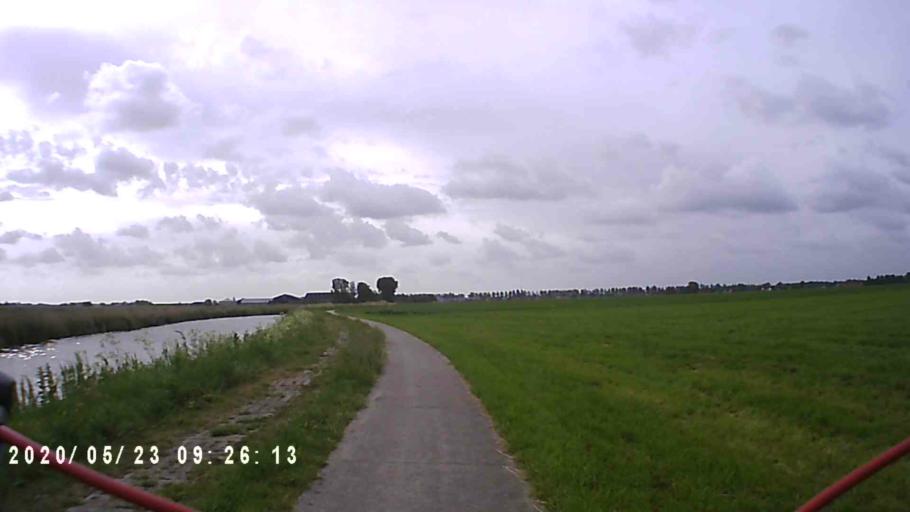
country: NL
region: Groningen
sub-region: Gemeente Bedum
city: Bedum
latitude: 53.2937
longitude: 6.6943
